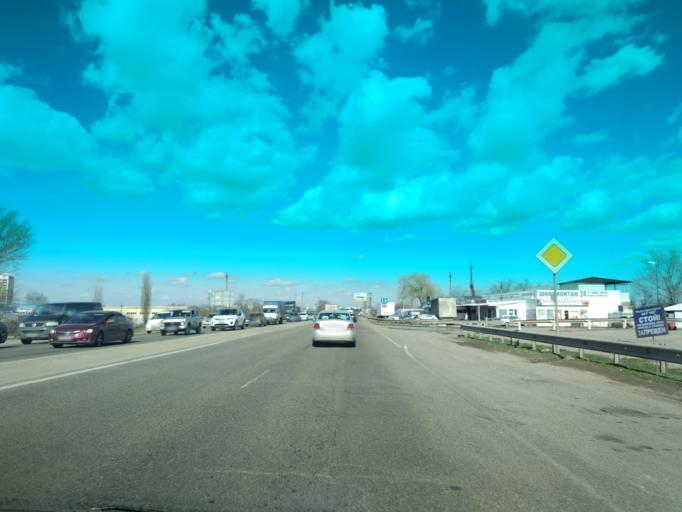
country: RU
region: Adygeya
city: Tlyustenkhabl'
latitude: 45.0001
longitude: 39.1152
